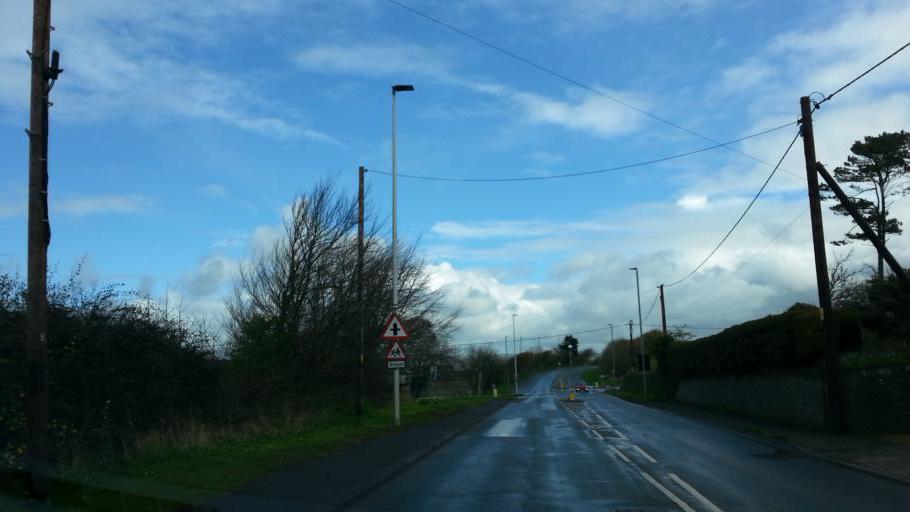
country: GB
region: England
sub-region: Devon
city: Appledore
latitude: 51.0574
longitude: -4.1760
